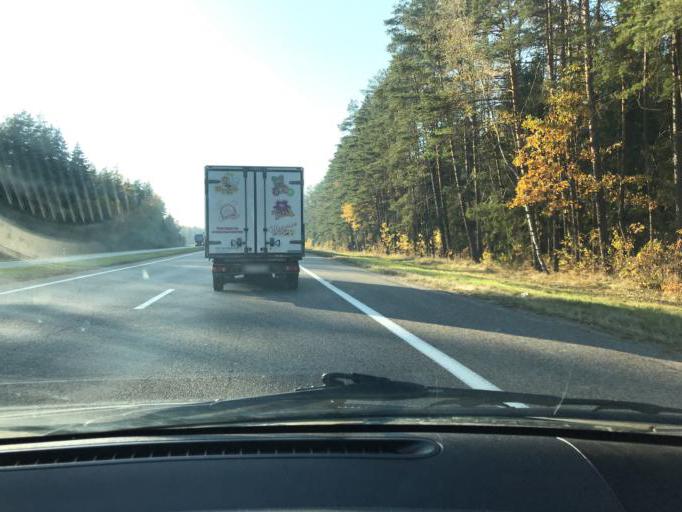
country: BY
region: Minsk
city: Loshnitsa
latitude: 54.2998
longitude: 28.9386
